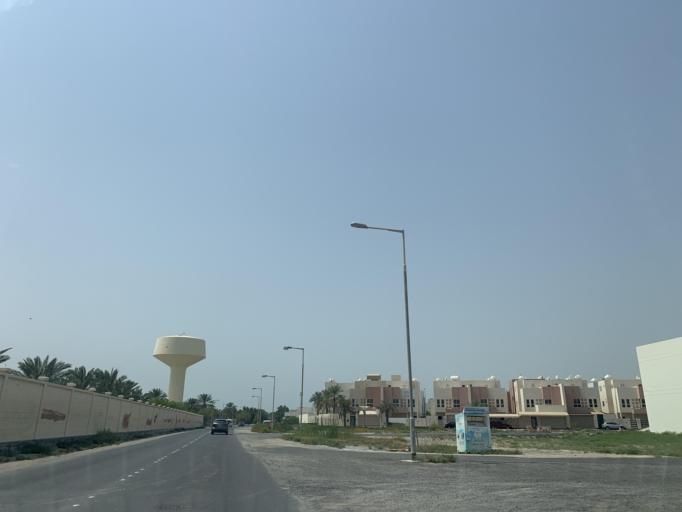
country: BH
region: Central Governorate
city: Madinat Hamad
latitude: 26.1389
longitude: 50.4611
